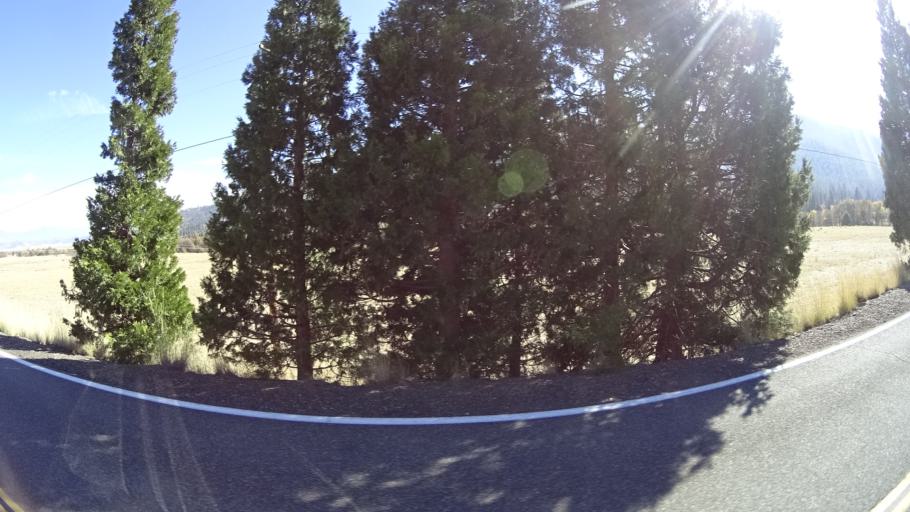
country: US
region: California
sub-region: Siskiyou County
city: Weed
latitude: 41.4857
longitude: -122.5698
